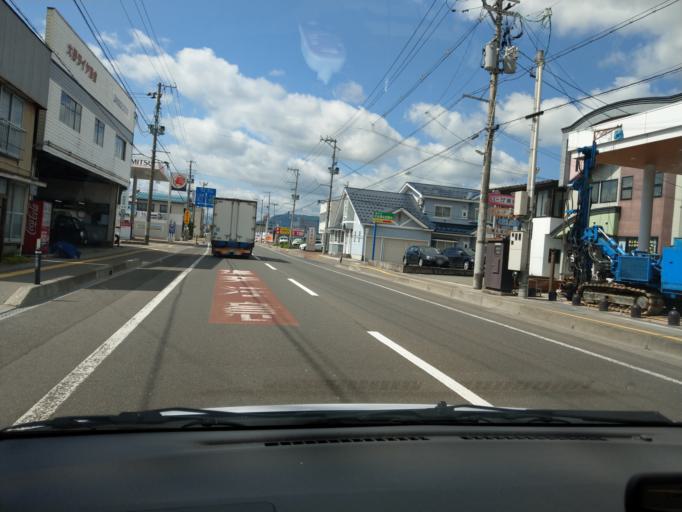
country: JP
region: Akita
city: Yuzawa
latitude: 39.1711
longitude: 140.4909
